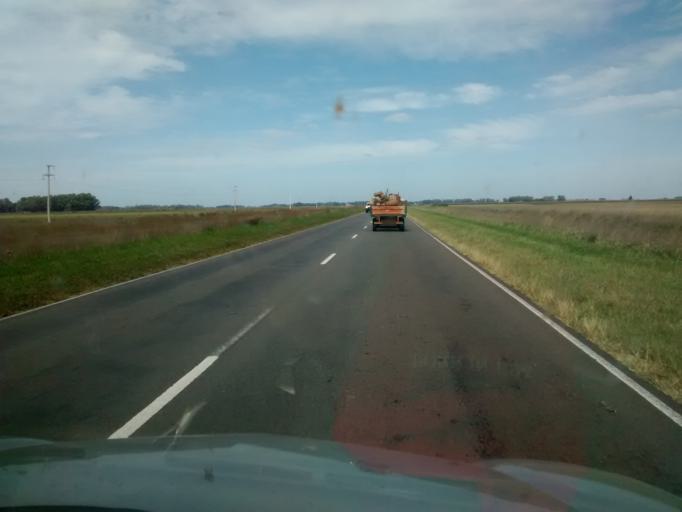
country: AR
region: Buenos Aires
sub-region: Partido de Ayacucho
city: Ayacucho
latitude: -37.0882
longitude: -58.5465
